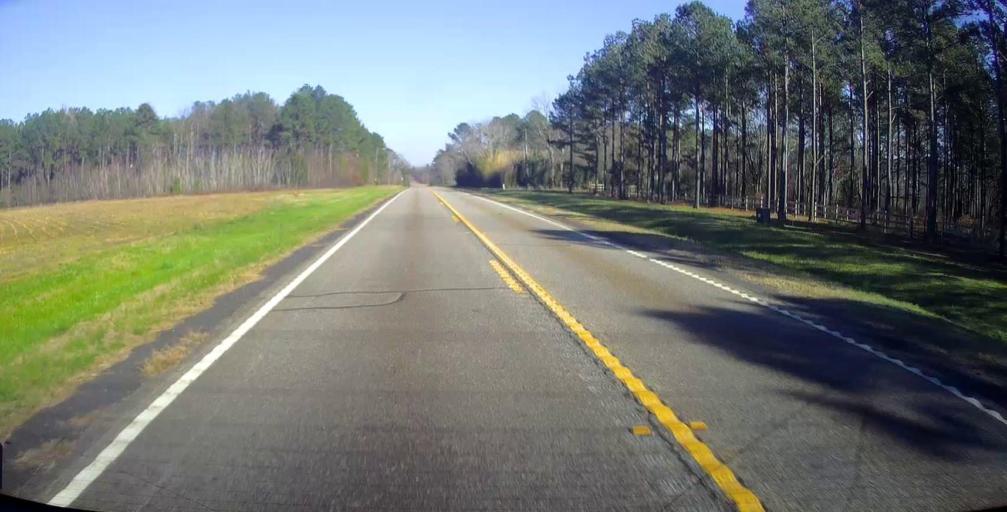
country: US
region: Georgia
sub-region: Schley County
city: Ellaville
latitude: 32.1822
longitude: -84.2614
